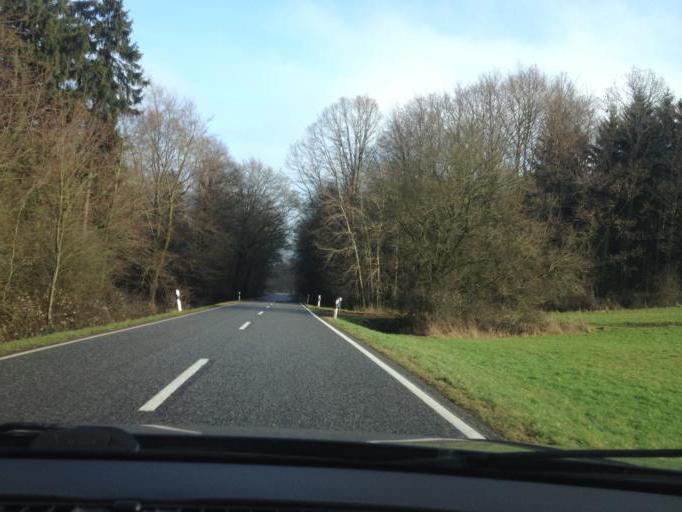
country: DE
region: Saarland
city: Mainzweiler
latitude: 49.4283
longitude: 7.1035
